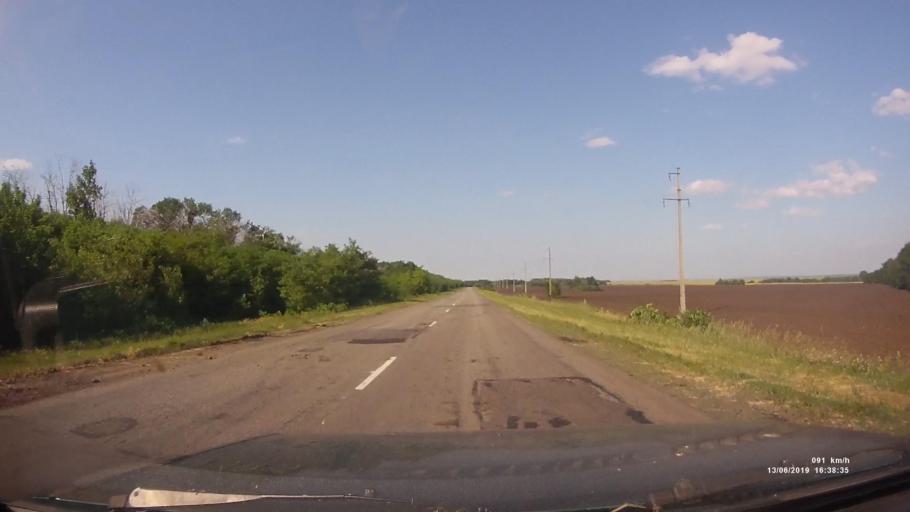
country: RU
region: Rostov
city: Kazanskaya
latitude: 49.9203
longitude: 41.3260
